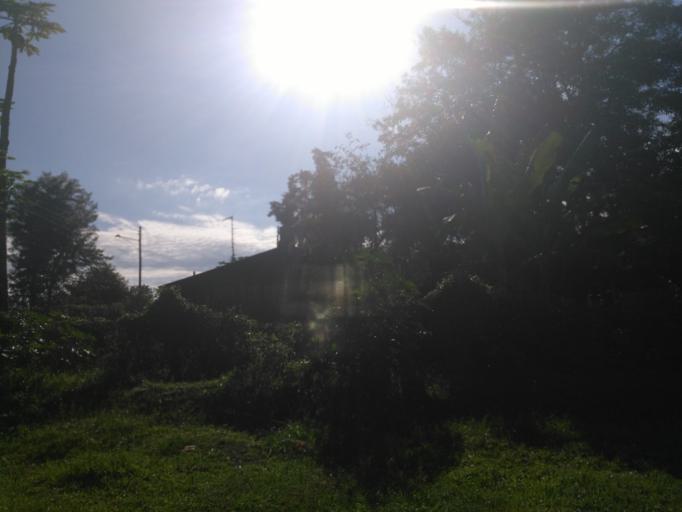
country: UG
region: Eastern Region
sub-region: Jinja District
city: Jinja
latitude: 0.4456
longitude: 33.1914
